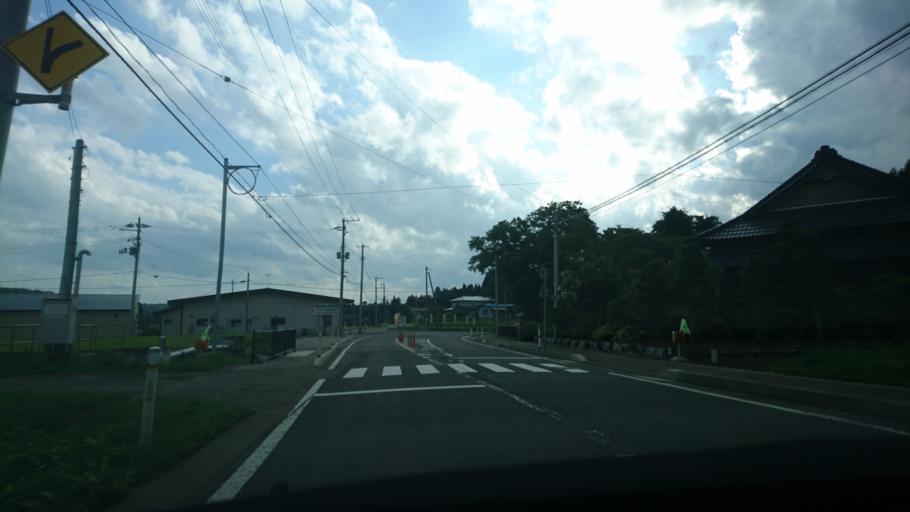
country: JP
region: Iwate
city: Kitakami
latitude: 39.3140
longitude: 141.1591
